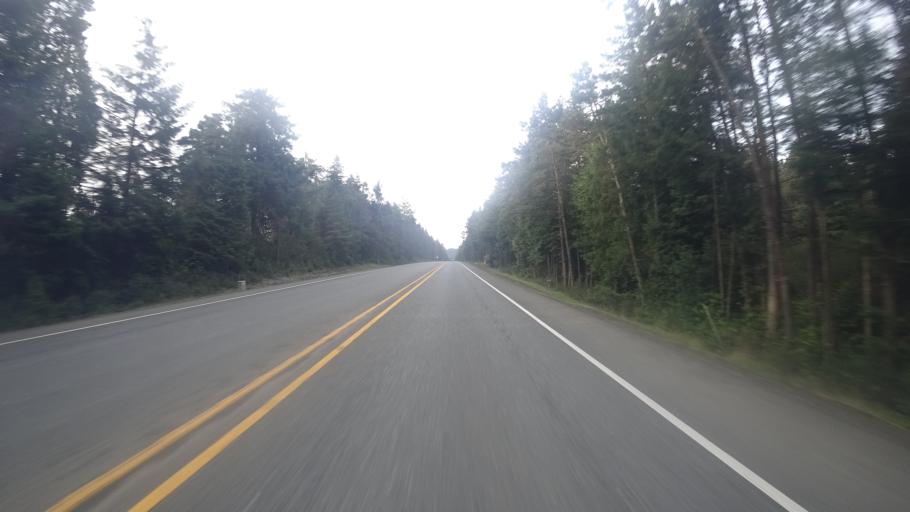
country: US
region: Oregon
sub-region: Coos County
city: Lakeside
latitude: 43.5073
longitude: -124.2178
